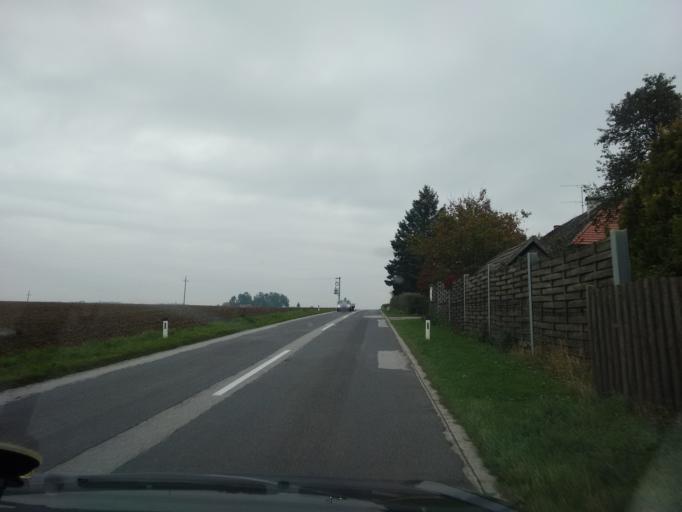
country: AT
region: Upper Austria
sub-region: Politischer Bezirk Kirchdorf an der Krems
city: Kremsmunster
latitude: 48.0347
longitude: 14.0909
